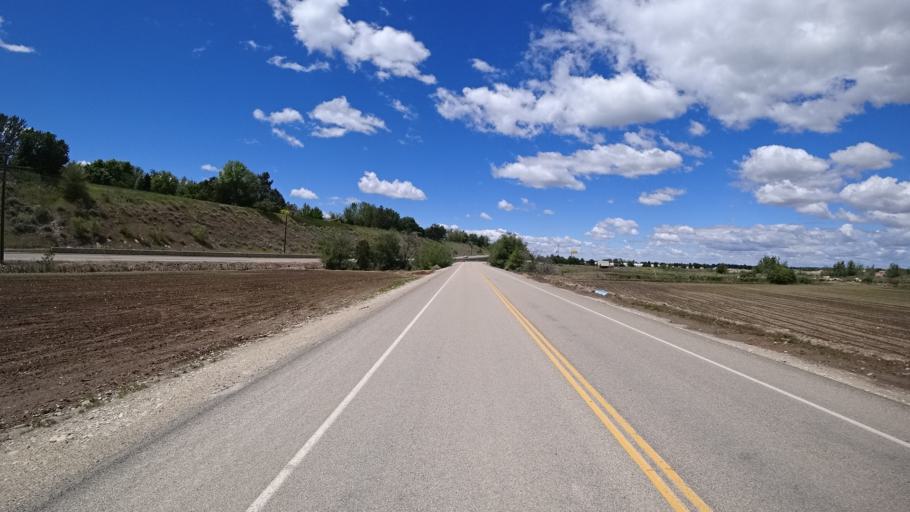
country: US
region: Idaho
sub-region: Ada County
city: Eagle
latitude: 43.6592
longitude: -116.3083
